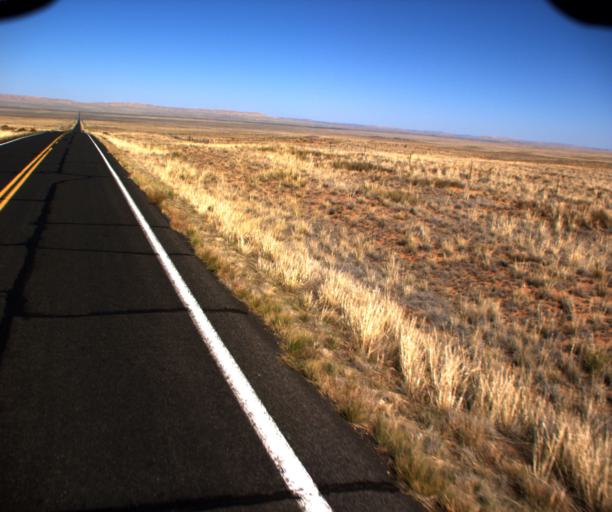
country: US
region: Arizona
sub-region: Navajo County
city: First Mesa
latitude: 35.6416
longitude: -110.4860
